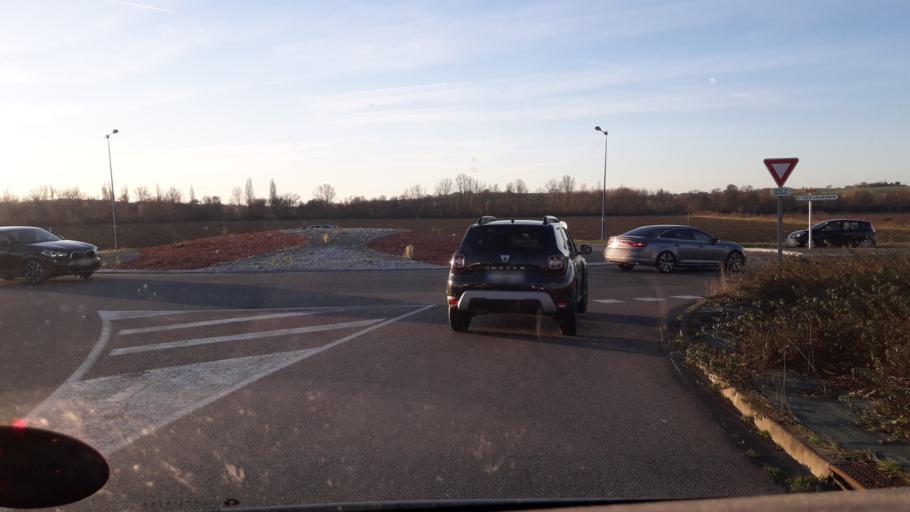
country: FR
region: Midi-Pyrenees
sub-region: Departement du Gers
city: Pujaudran
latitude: 43.6010
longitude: 1.0676
